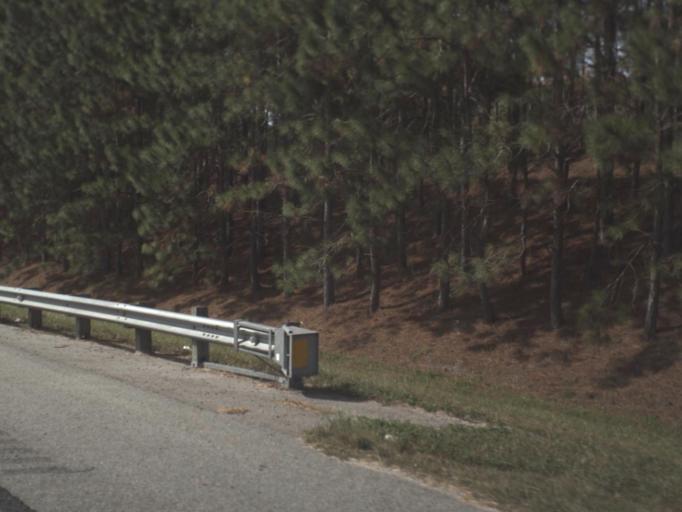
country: US
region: Florida
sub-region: Orange County
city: Gotha
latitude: 28.5406
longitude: -81.5219
